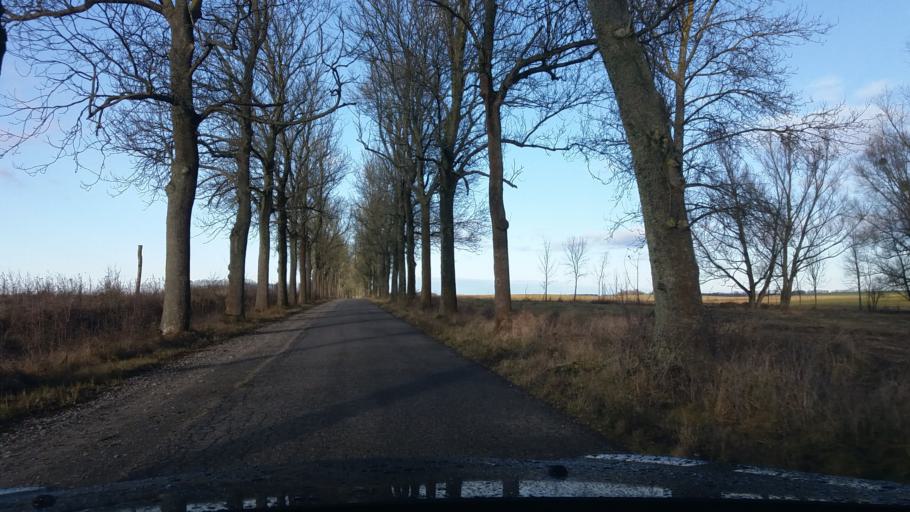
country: PL
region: West Pomeranian Voivodeship
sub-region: Powiat choszczenski
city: Drawno
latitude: 53.1855
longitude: 15.7974
